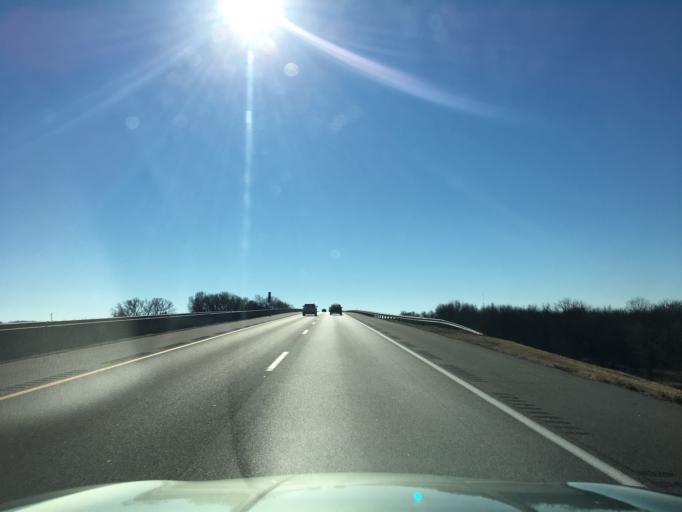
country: US
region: Kansas
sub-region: Sumner County
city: Belle Plaine
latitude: 37.3543
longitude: -97.3222
